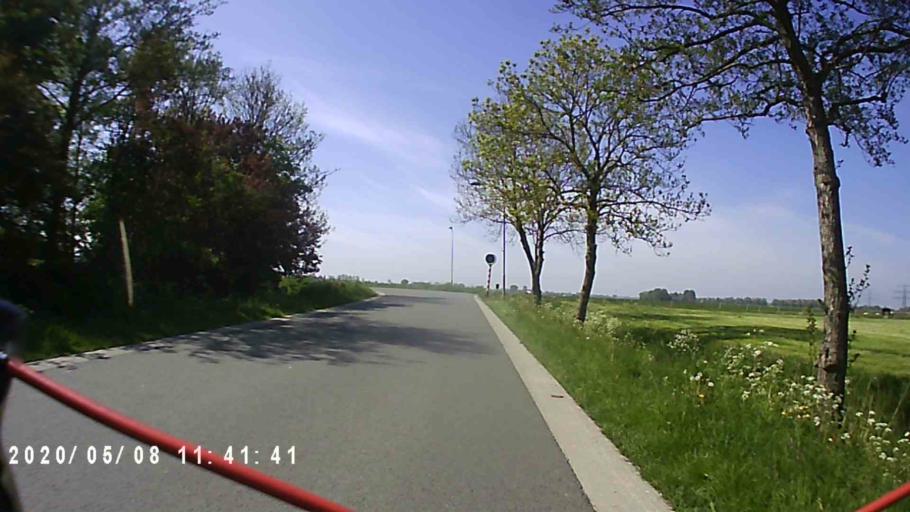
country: NL
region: Groningen
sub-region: Gemeente Bedum
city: Bedum
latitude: 53.3265
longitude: 6.6859
